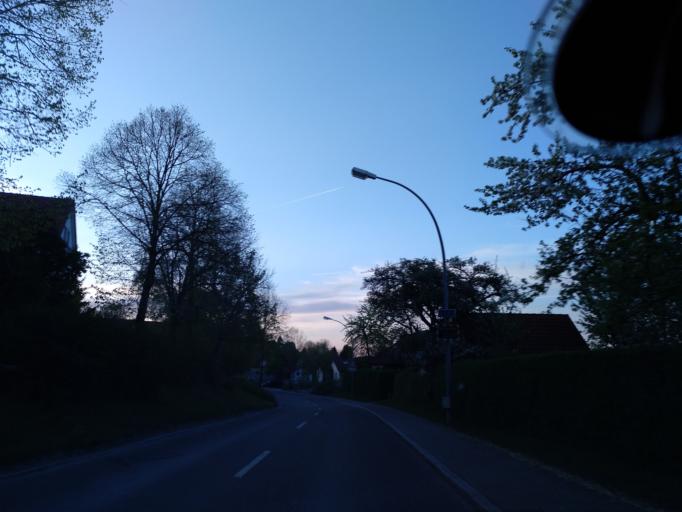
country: DE
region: Baden-Wuerttemberg
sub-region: Regierungsbezirk Stuttgart
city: Satteldorf
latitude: 49.1692
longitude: 10.0787
